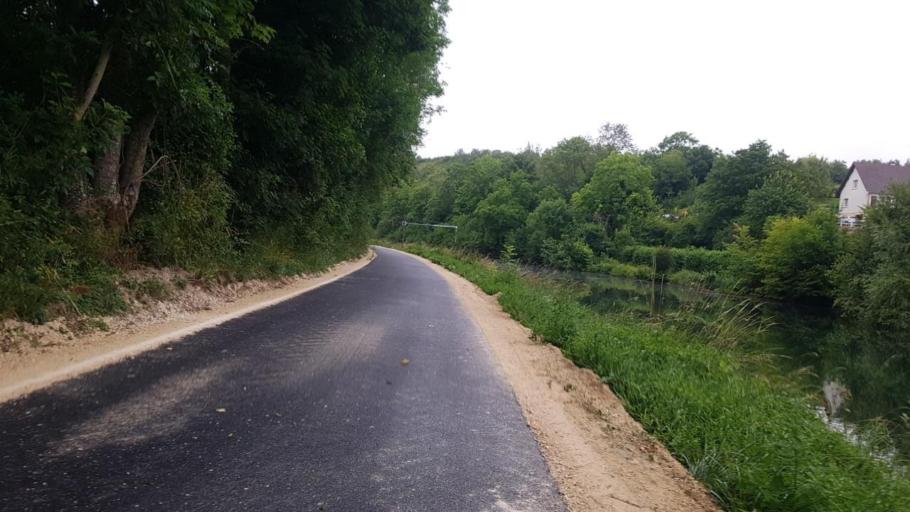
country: FR
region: Champagne-Ardenne
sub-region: Departement de la Marne
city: Vitry-le-Francois
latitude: 48.7928
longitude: 4.5325
